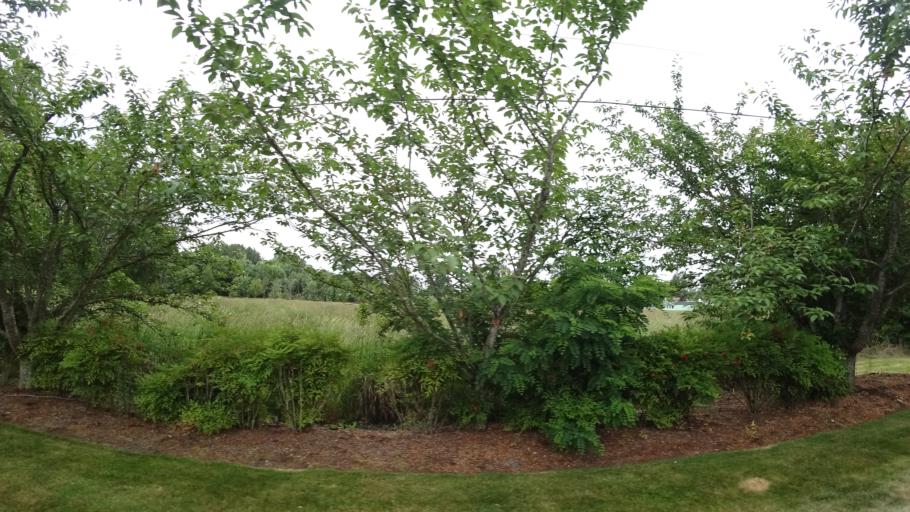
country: US
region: Washington
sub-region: Clark County
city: Vancouver
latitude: 45.5938
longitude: -122.6503
